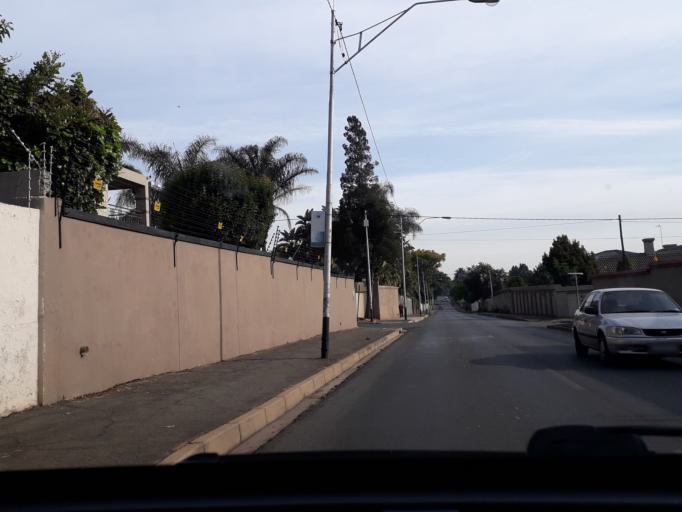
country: ZA
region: Gauteng
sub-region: City of Johannesburg Metropolitan Municipality
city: Johannesburg
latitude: -26.1536
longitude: 28.0964
